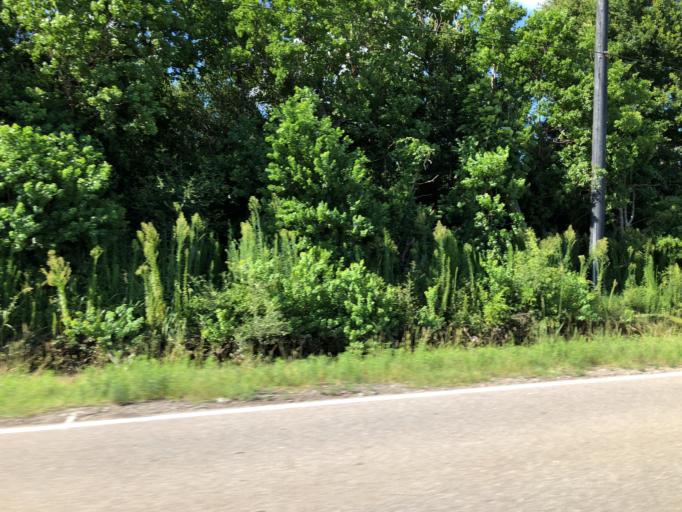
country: US
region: Texas
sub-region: Harris County
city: Katy
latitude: 29.8315
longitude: -95.8005
